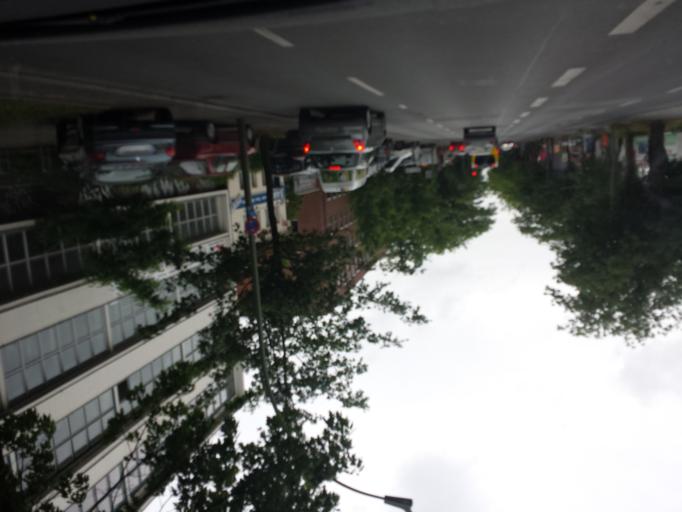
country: DE
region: Berlin
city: Mariendorf
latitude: 52.4286
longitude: 13.3754
